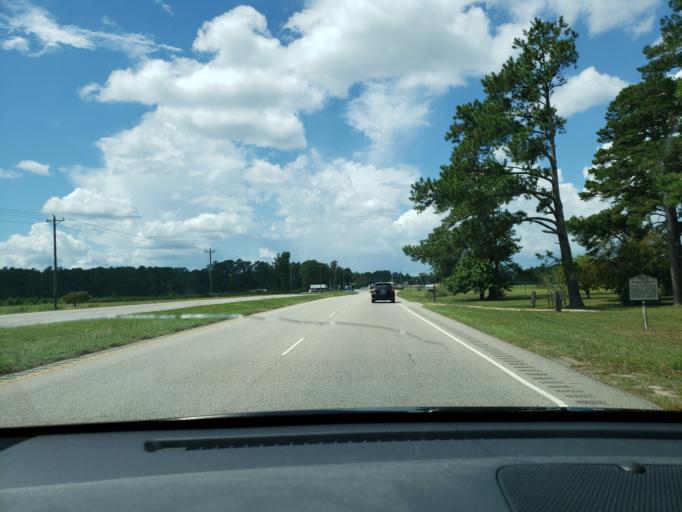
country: US
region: North Carolina
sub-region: Bladen County
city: Bladenboro
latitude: 34.7304
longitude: -78.7824
